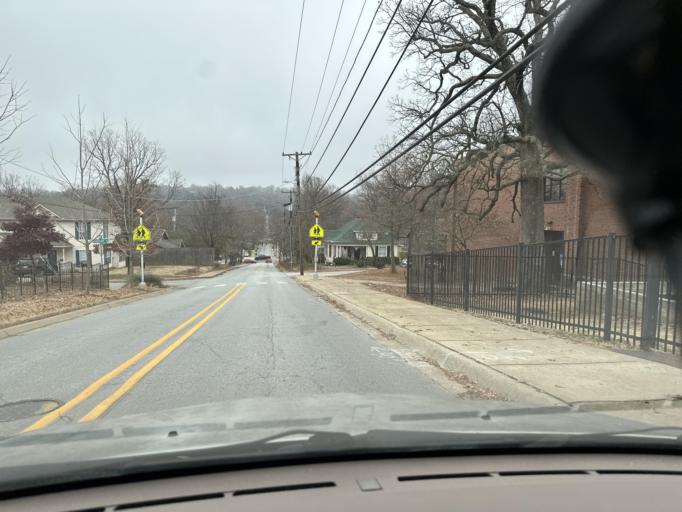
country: US
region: Arkansas
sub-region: Washington County
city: Fayetteville
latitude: 36.0700
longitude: -94.1595
